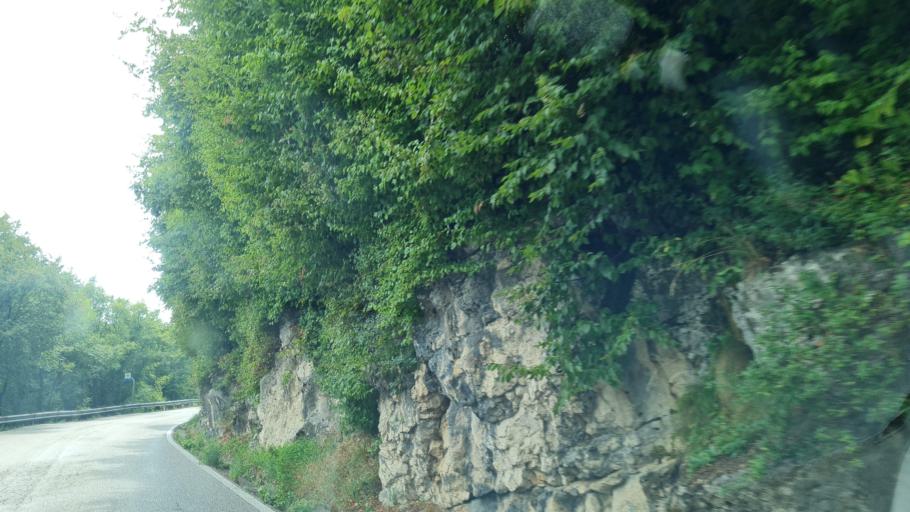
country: IT
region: Veneto
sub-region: Provincia di Vicenza
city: Conco
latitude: 45.7881
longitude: 11.6455
